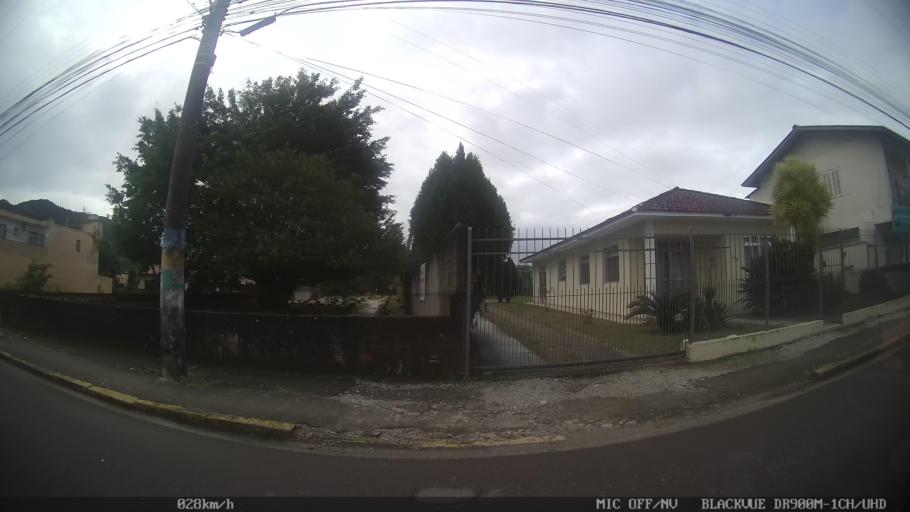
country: BR
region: Santa Catarina
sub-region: Biguacu
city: Biguacu
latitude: -27.4917
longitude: -48.6546
